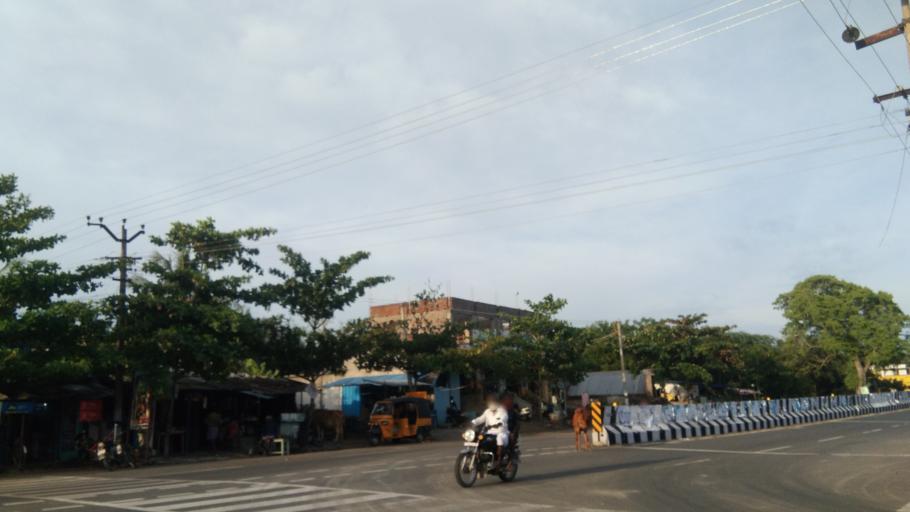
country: IN
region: Tamil Nadu
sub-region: Villupuram
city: Vikravandi
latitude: 12.0785
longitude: 79.6587
